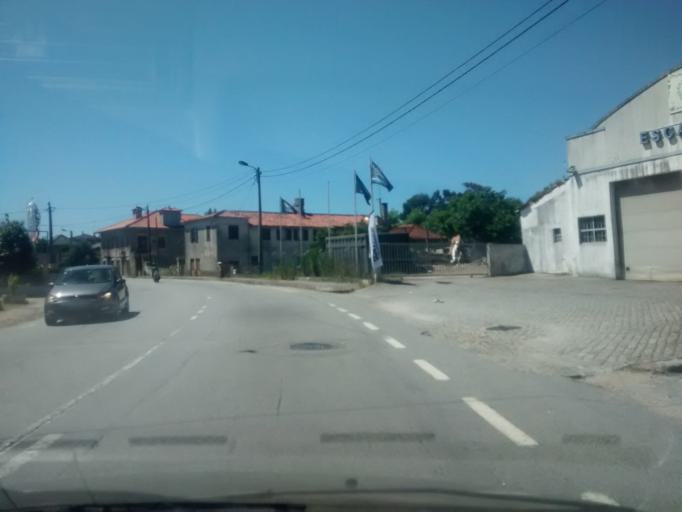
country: PT
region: Braga
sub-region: Braga
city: Oliveira
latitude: 41.5330
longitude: -8.4930
